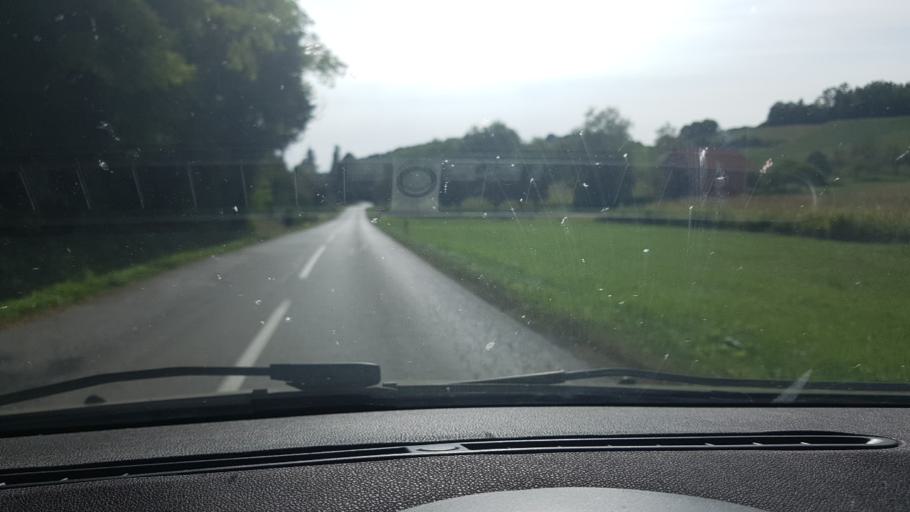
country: HR
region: Krapinsko-Zagorska
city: Zlatar
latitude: 46.1202
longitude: 16.0997
